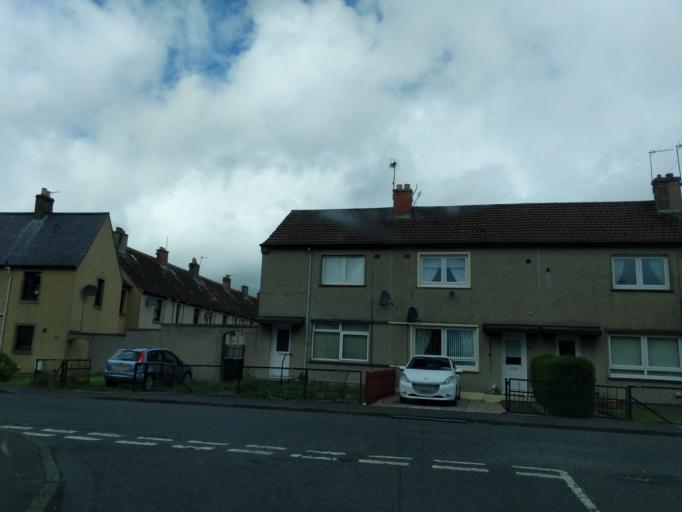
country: GB
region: Scotland
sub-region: Midlothian
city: Penicuik
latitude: 55.8307
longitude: -3.2216
